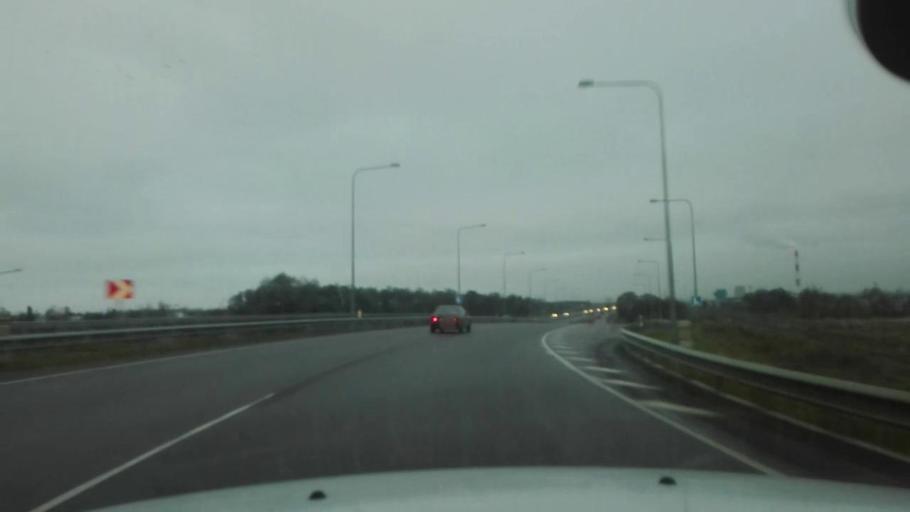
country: EE
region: Harju
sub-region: Joelaehtme vald
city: Loo
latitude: 59.4521
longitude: 24.9821
